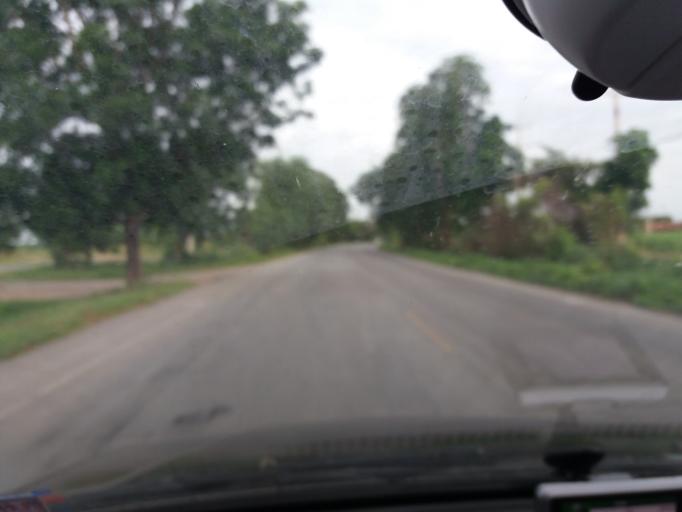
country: TH
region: Kanchanaburi
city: Huai Krachao
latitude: 14.3340
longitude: 99.7656
